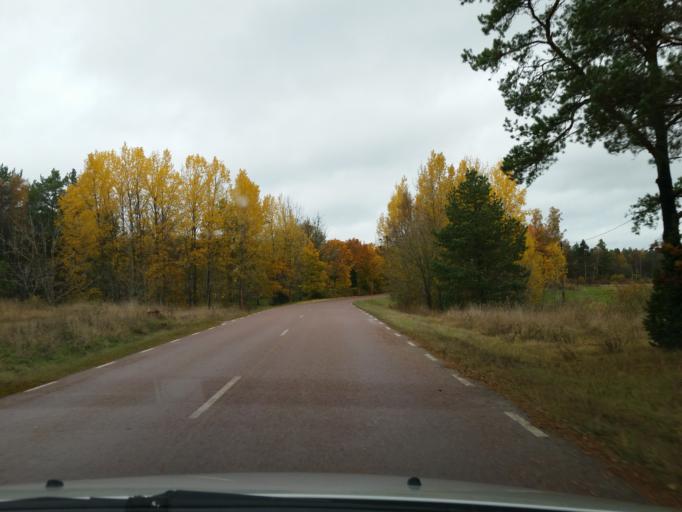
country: AX
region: Alands landsbygd
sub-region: Lumparland
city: Lumparland
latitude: 60.1241
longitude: 20.2406
